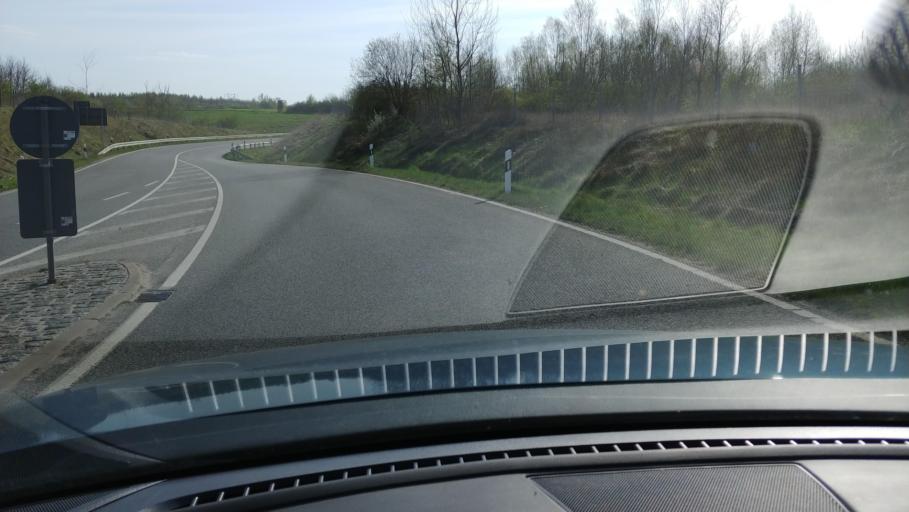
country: DE
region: Mecklenburg-Vorpommern
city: Seehof
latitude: 53.6809
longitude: 11.3990
